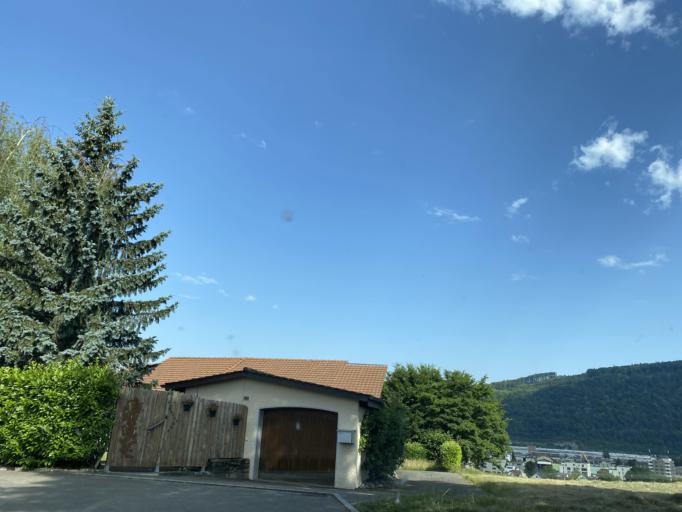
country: CH
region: Aargau
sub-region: Bezirk Zofingen
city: Rothrist
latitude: 47.3007
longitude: 7.8800
